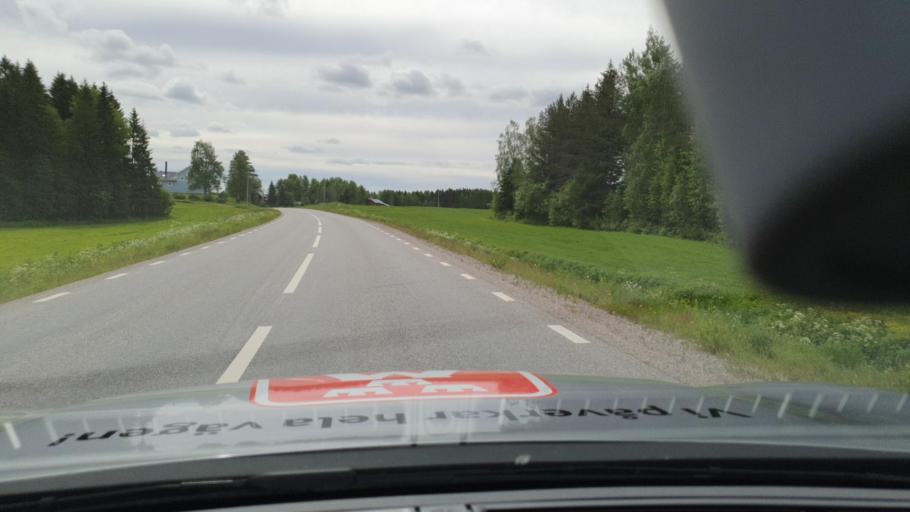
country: SE
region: Norrbotten
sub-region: Kalix Kommun
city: Kalix
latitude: 65.9460
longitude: 23.4556
